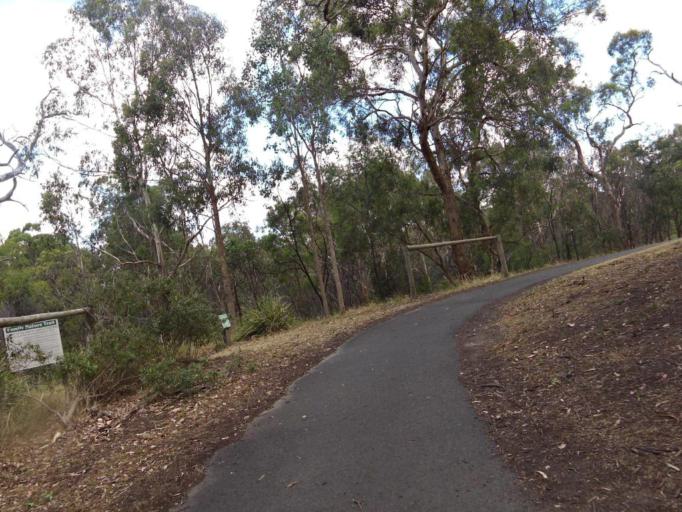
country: AU
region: Victoria
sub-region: Nillumbik
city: Eltham
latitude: -37.7341
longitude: 145.1431
